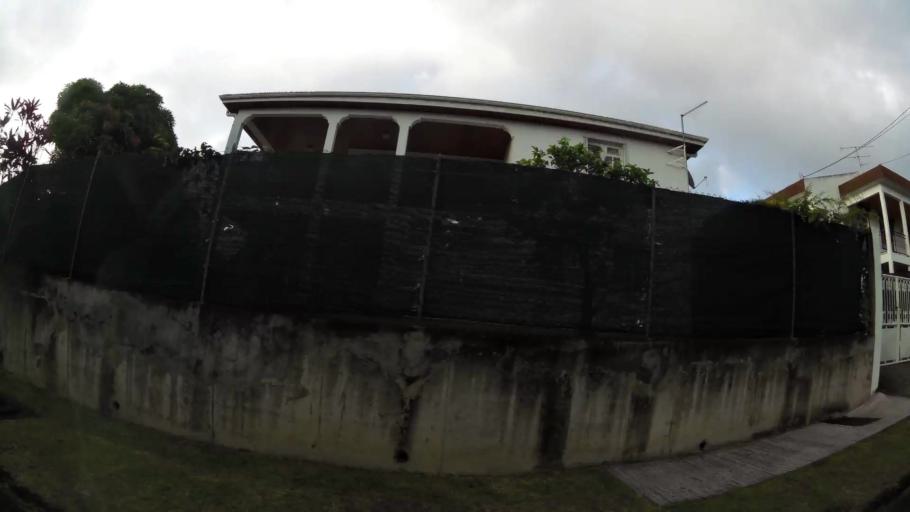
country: MQ
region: Martinique
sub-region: Martinique
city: Fort-de-France
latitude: 14.6205
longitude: -61.0837
